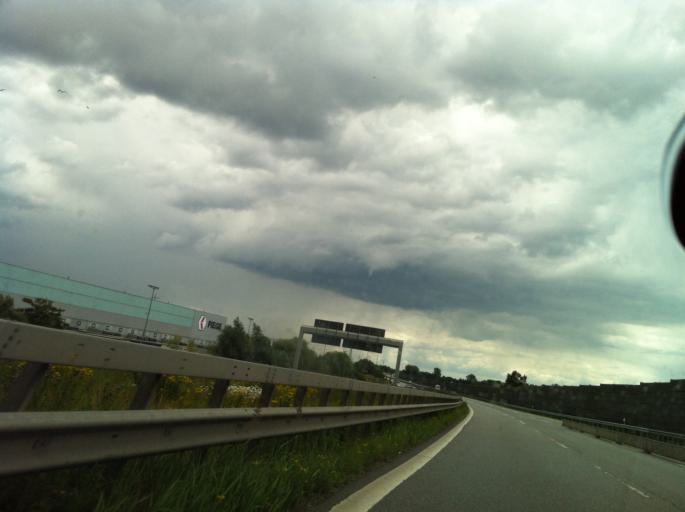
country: DE
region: Hamburg
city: Rothenburgsort
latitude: 53.5074
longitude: 10.0818
